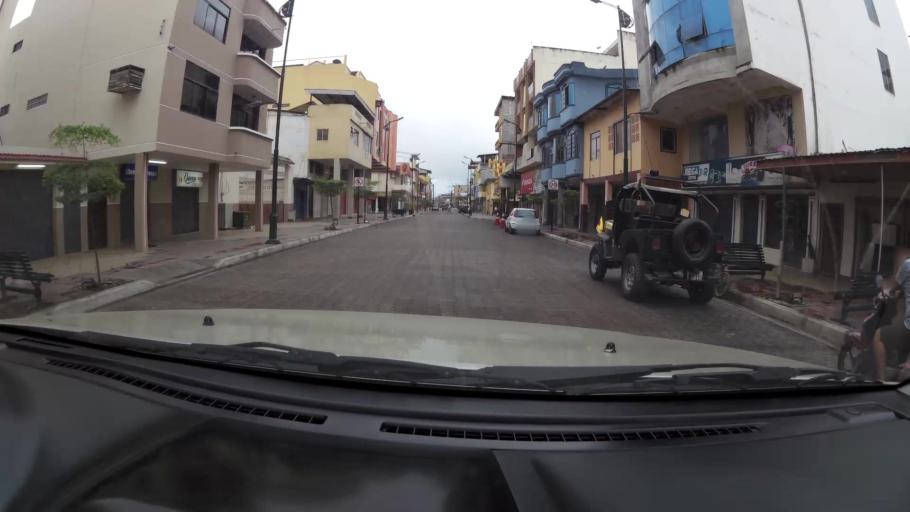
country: EC
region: El Oro
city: Pasaje
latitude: -3.3271
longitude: -79.8093
